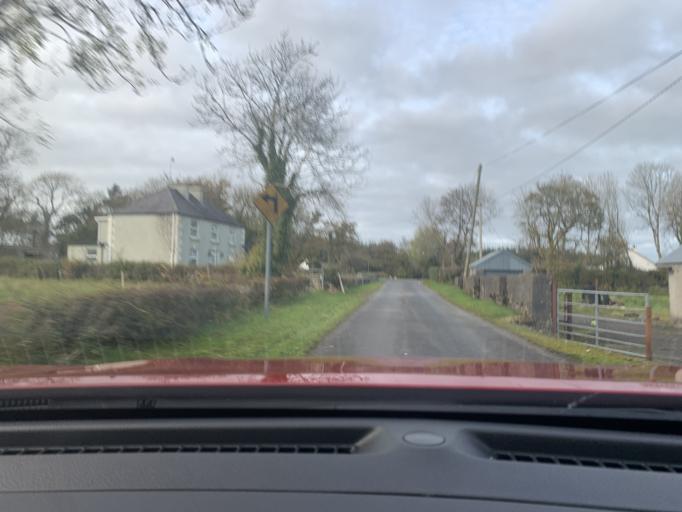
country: IE
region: Connaught
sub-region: Roscommon
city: Ballaghaderreen
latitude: 54.0103
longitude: -8.6073
